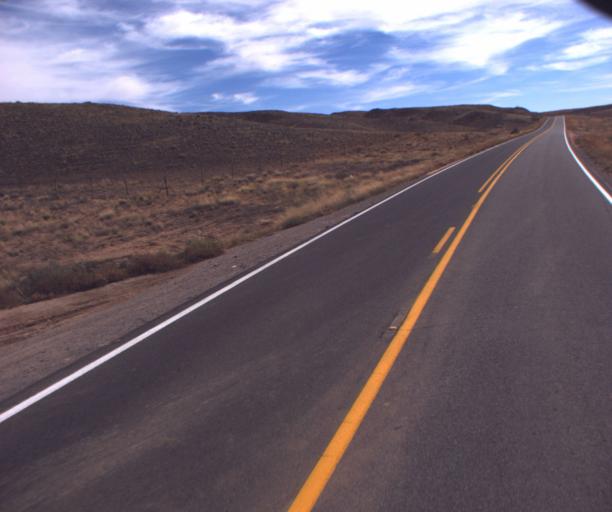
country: US
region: Arizona
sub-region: Navajo County
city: Kayenta
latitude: 36.8252
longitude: -110.2380
